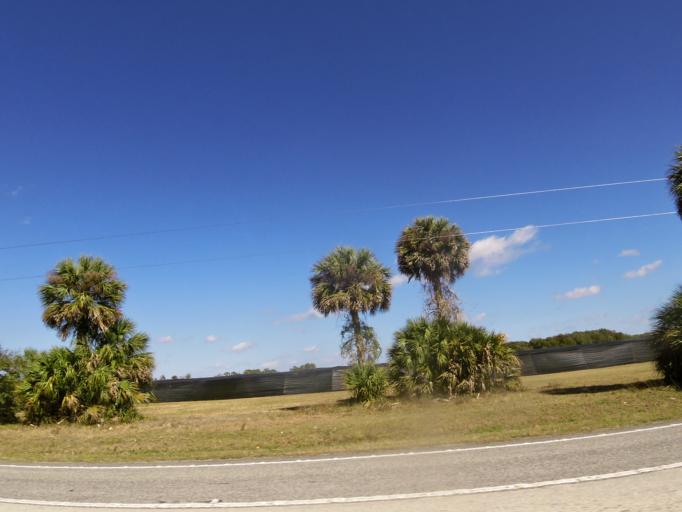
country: US
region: Florida
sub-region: Volusia County
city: Pierson
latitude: 29.2078
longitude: -81.4471
